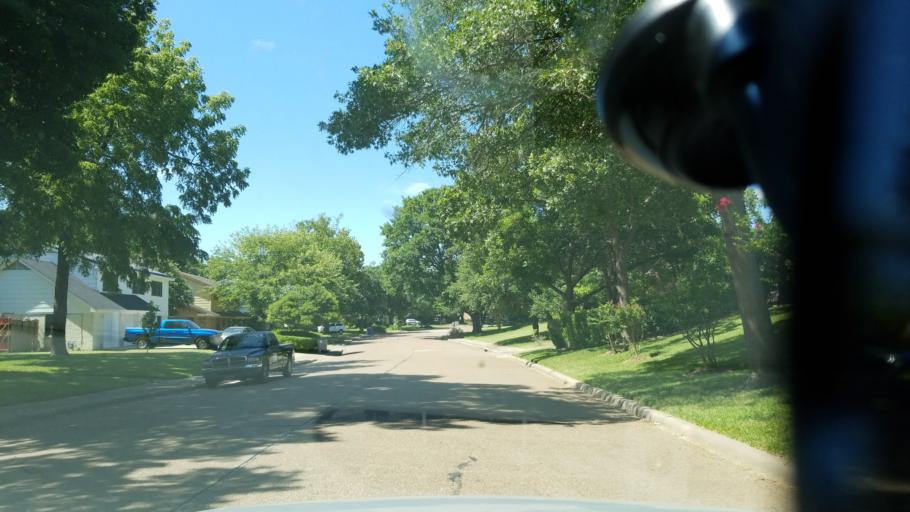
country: US
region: Texas
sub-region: Dallas County
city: Cockrell Hill
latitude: 32.6802
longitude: -96.8314
